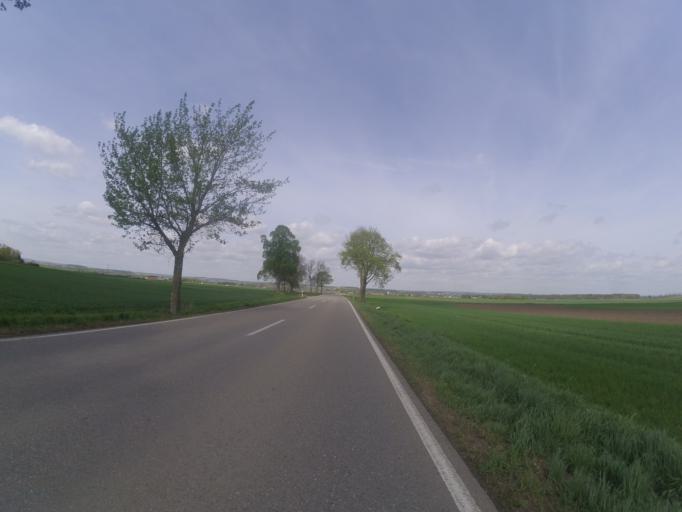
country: DE
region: Baden-Wuerttemberg
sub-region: Tuebingen Region
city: Ersingen
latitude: 48.2776
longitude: 9.8597
